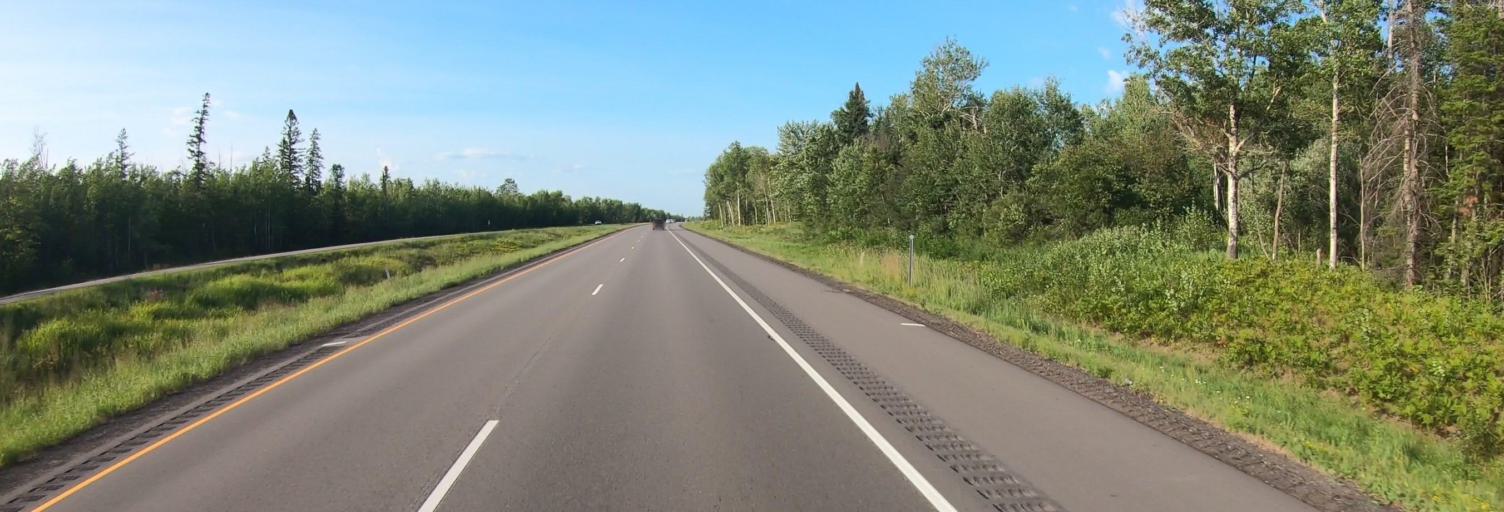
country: US
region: Minnesota
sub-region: Saint Louis County
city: Eveleth
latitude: 47.2672
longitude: -92.4798
